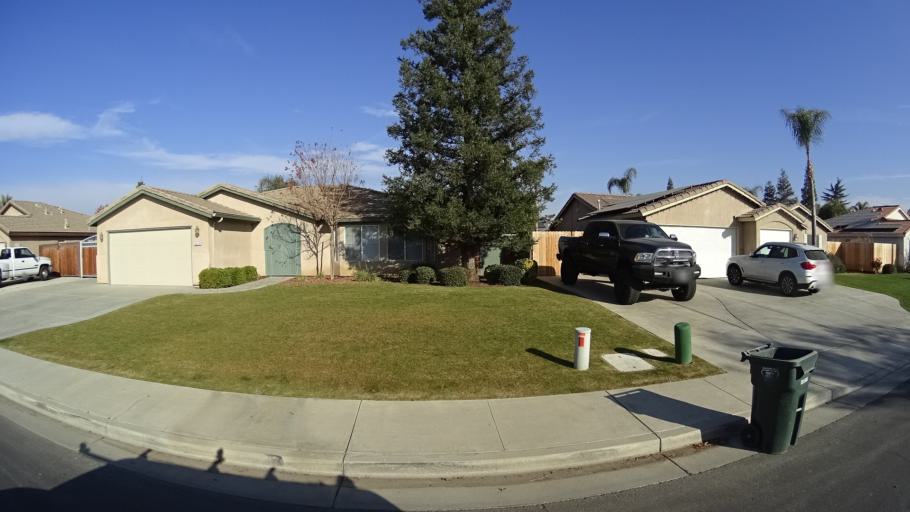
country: US
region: California
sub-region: Kern County
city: Oildale
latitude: 35.4053
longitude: -119.0627
